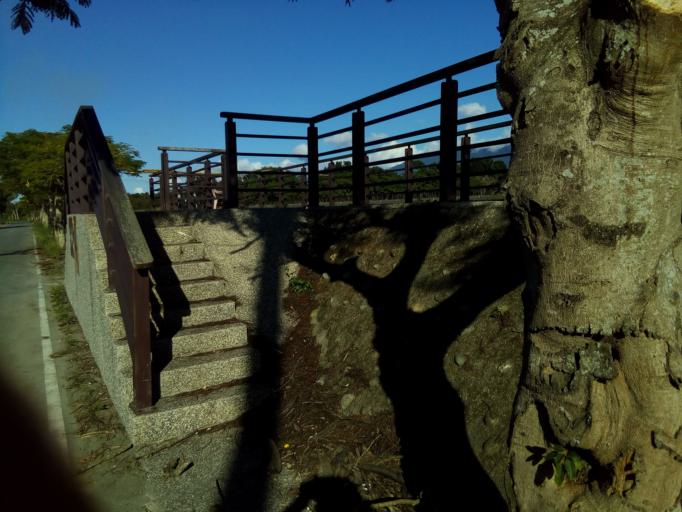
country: TW
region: Taiwan
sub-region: Taitung
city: Taitung
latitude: 23.0344
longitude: 121.1694
